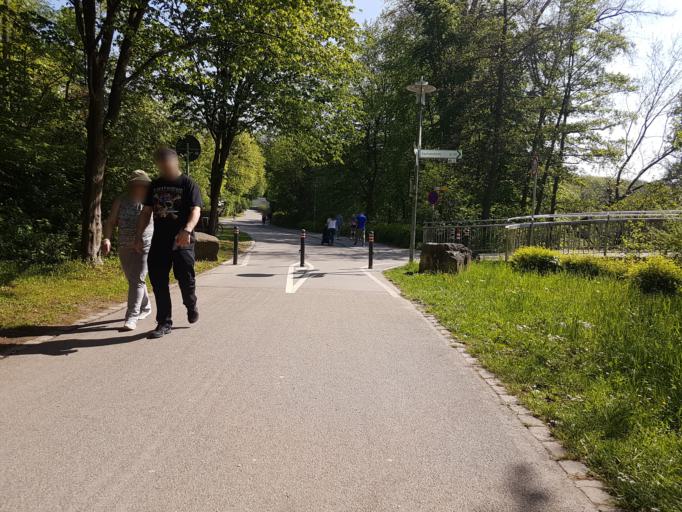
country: DE
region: Baden-Wuerttemberg
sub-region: Regierungsbezirk Stuttgart
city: Bietigheim-Bissingen
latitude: 48.9510
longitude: 9.1309
